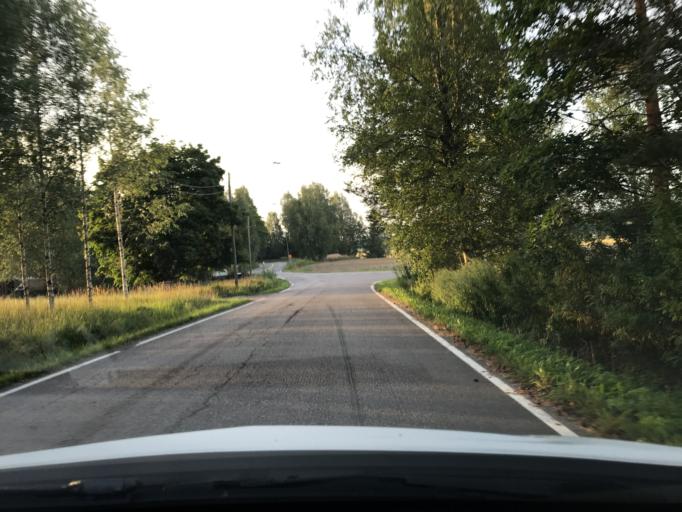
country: FI
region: Uusimaa
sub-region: Helsinki
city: Vihti
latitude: 60.4309
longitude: 24.5231
